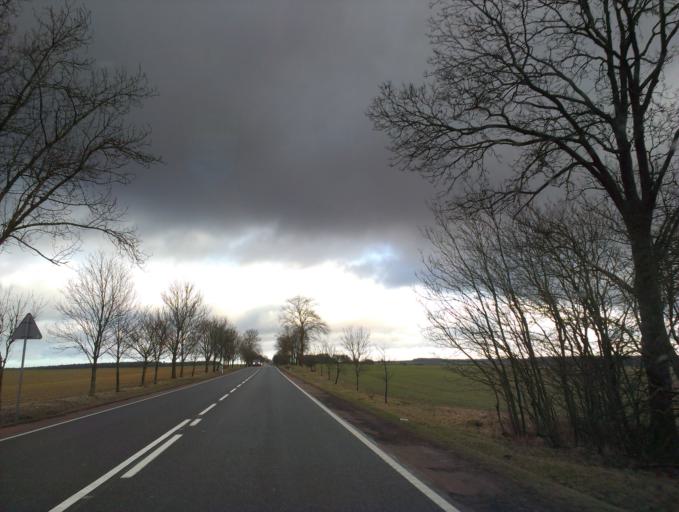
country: PL
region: Pomeranian Voivodeship
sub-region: Powiat czluchowski
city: Debrzno
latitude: 53.6283
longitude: 17.2453
